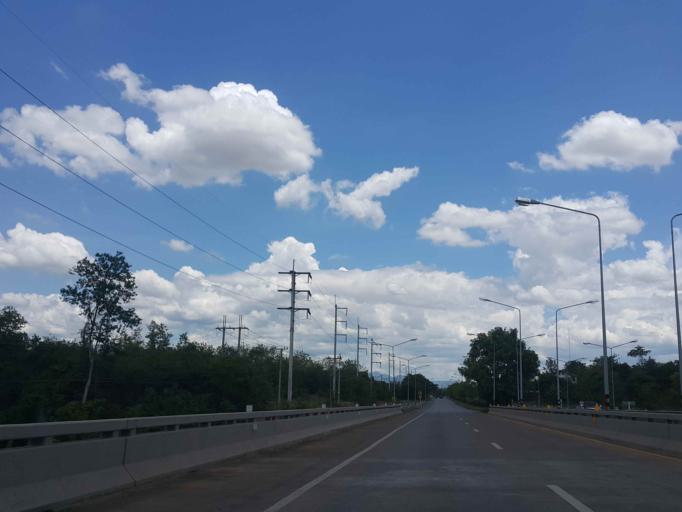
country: TH
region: Phrae
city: Nong Muang Khai
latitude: 18.2175
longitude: 100.1981
